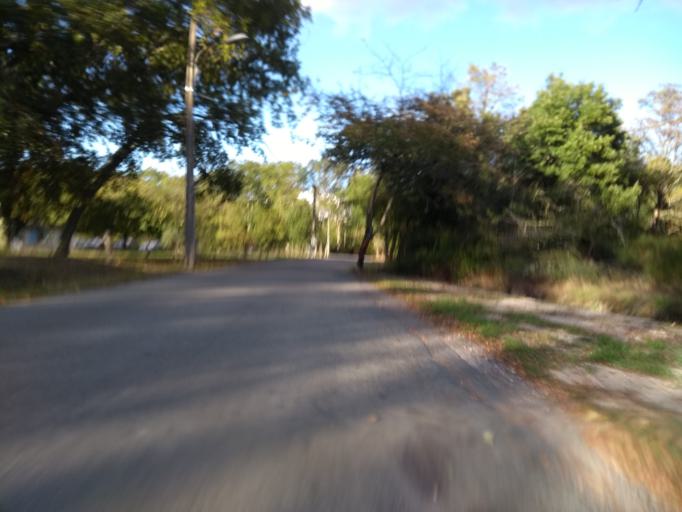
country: FR
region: Aquitaine
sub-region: Departement de la Gironde
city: Canejan
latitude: 44.7504
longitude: -0.6267
